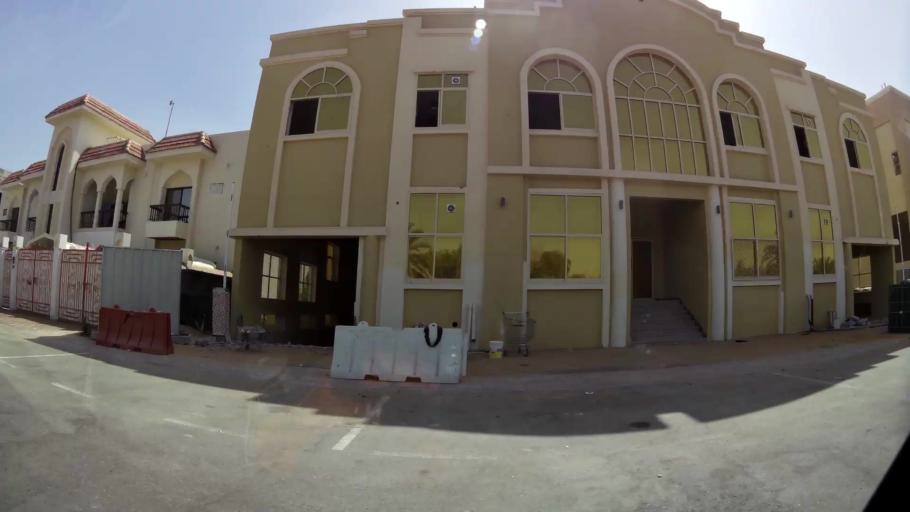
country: AE
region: Abu Dhabi
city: Al Ain
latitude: 24.2238
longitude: 55.6958
